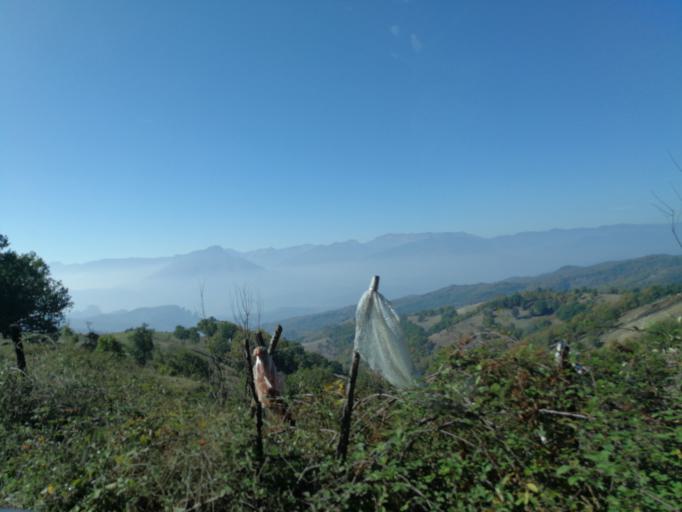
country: GR
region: Thessaly
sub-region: Trikala
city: Kastraki
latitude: 39.7705
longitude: 21.6631
